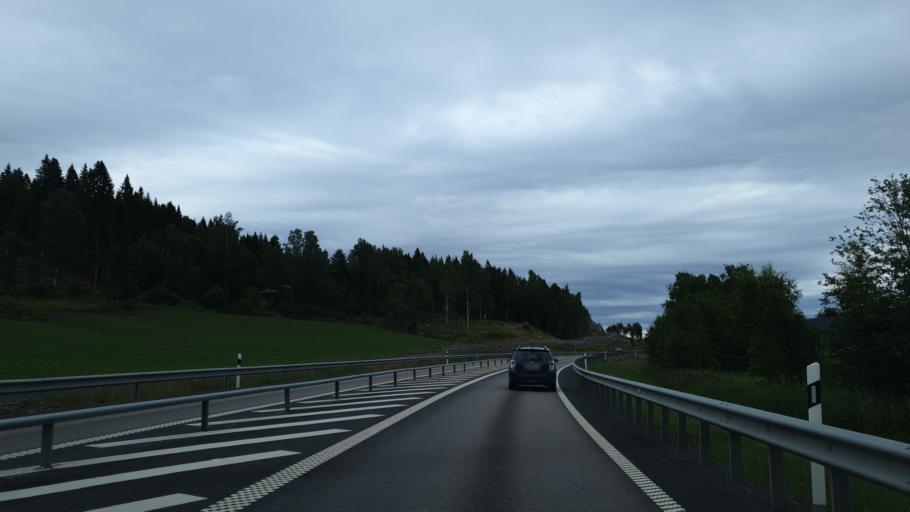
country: SE
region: Vaesternorrland
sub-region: Kramfors Kommun
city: Nordingra
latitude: 63.0082
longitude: 18.2731
